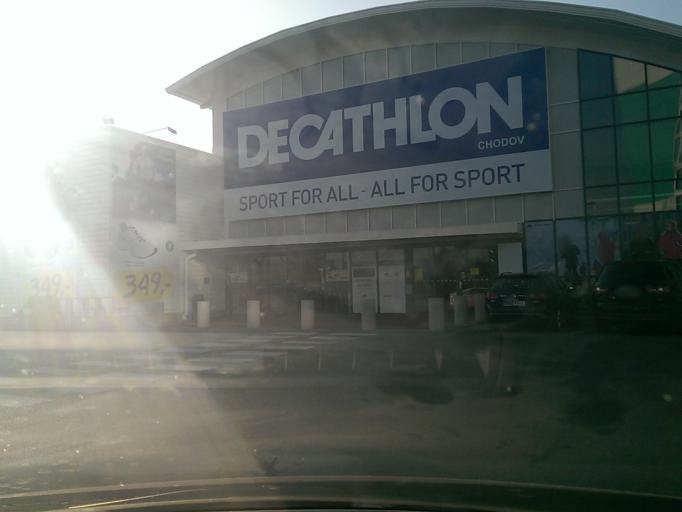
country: CZ
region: Central Bohemia
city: Vestec
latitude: 50.0368
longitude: 14.4922
